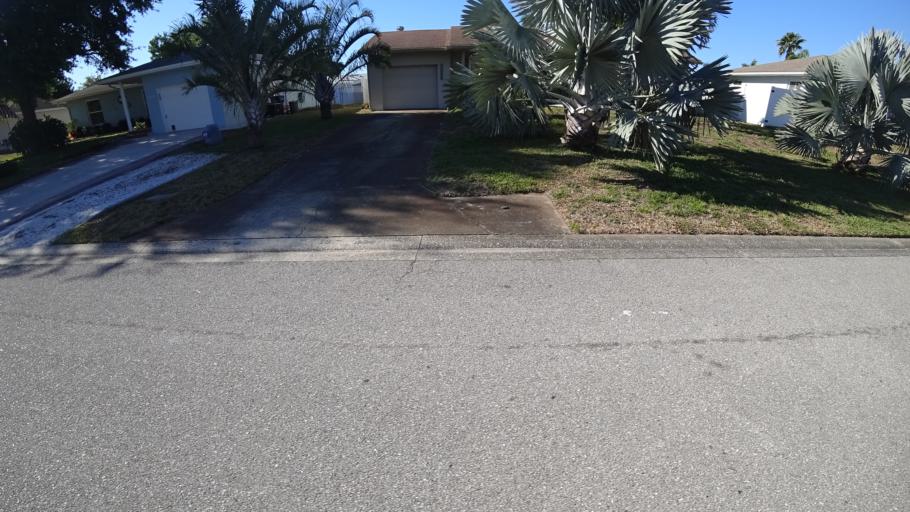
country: US
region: Florida
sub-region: Manatee County
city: Cortez
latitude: 27.4641
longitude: -82.6472
